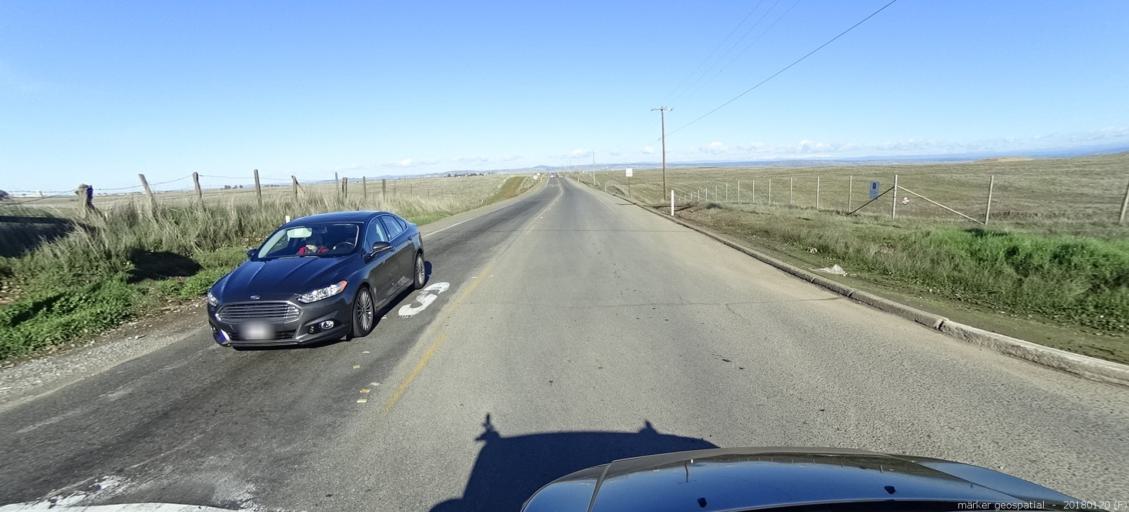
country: US
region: California
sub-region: Sacramento County
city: Rancho Murieta
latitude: 38.5210
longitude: -121.2019
